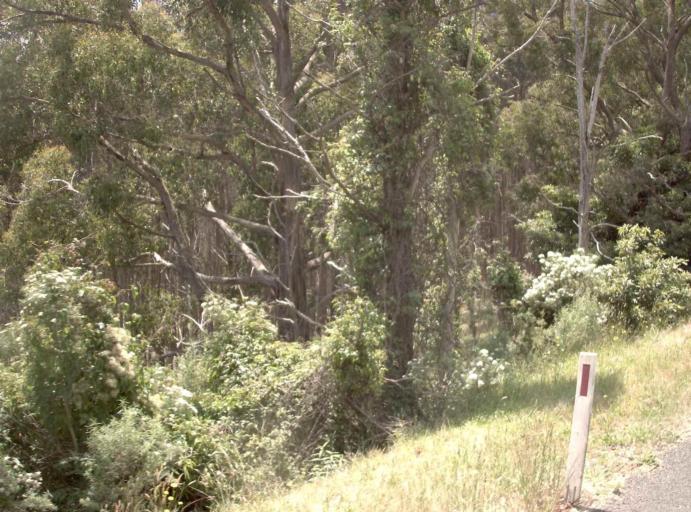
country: AU
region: Victoria
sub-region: Latrobe
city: Traralgon
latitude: -38.3580
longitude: 146.7498
